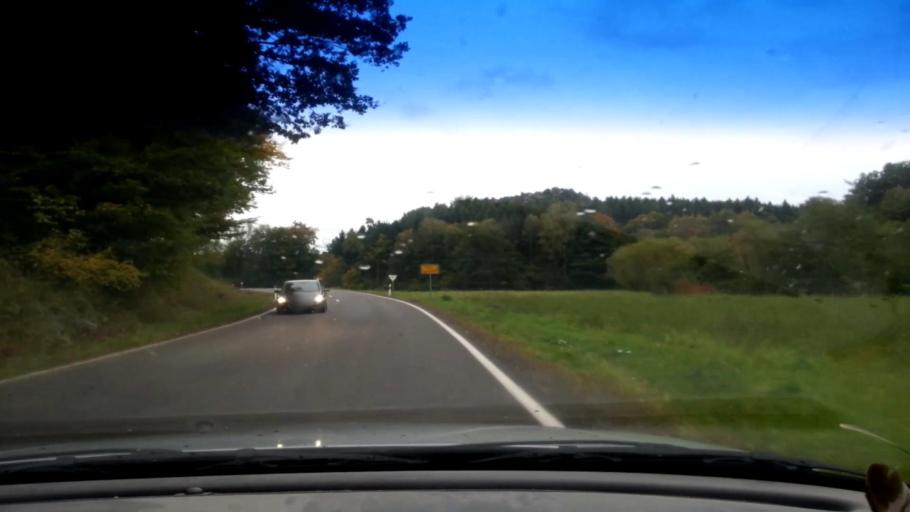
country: DE
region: Bavaria
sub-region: Regierungsbezirk Unterfranken
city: Stettfeld
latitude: 49.9978
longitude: 10.7484
